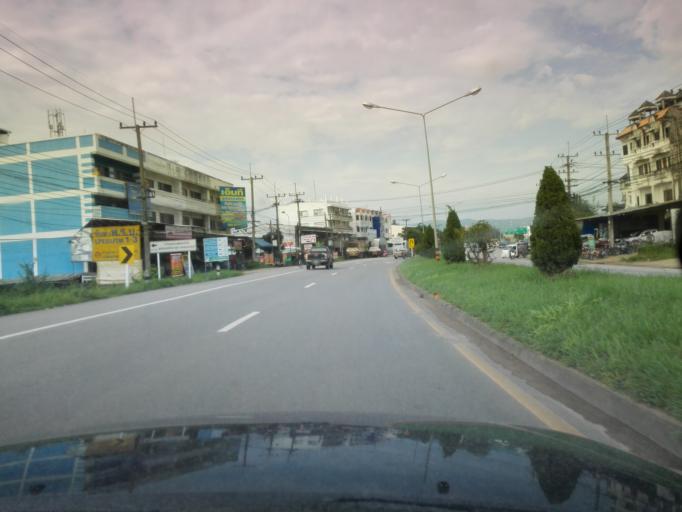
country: TH
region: Tak
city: Mae Sot
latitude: 16.7211
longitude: 98.5641
